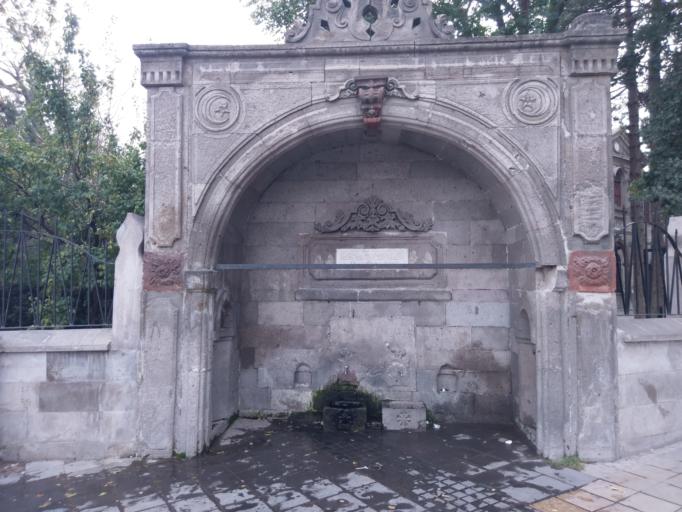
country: TR
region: Kayseri
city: Kayseri
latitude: 38.7169
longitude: 35.4894
